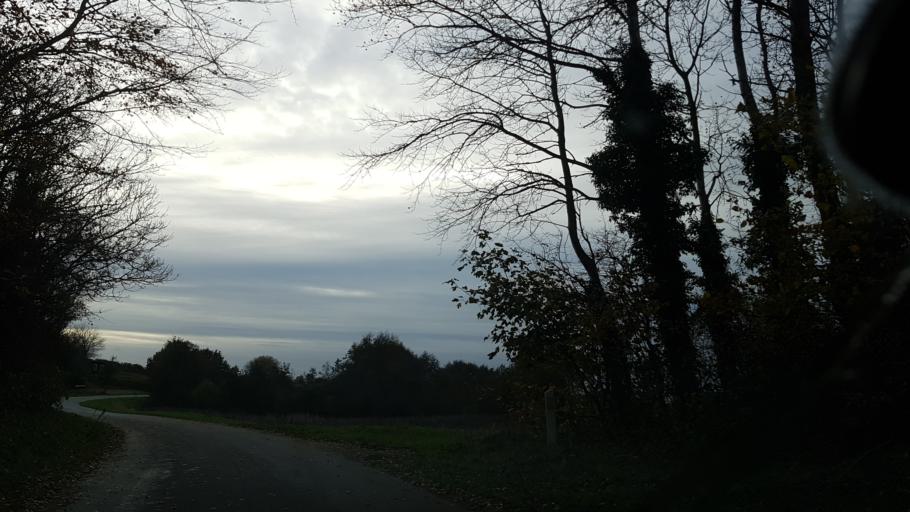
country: DK
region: South Denmark
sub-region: Haderslev Kommune
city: Vojens
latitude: 55.3072
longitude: 9.3901
